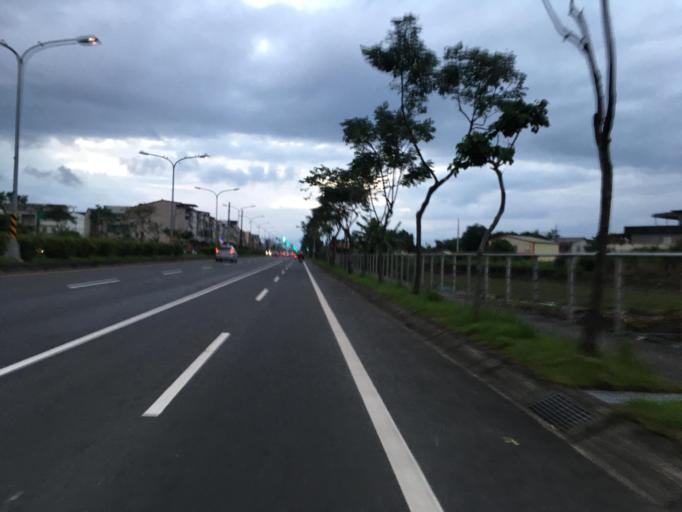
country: TW
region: Taiwan
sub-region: Yilan
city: Yilan
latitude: 24.6202
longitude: 121.8425
